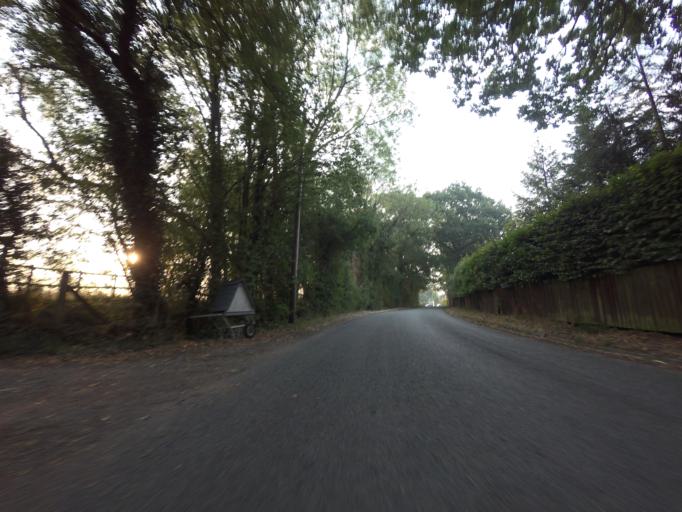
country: GB
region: England
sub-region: Kent
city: Lenham
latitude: 51.1827
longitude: 0.7199
